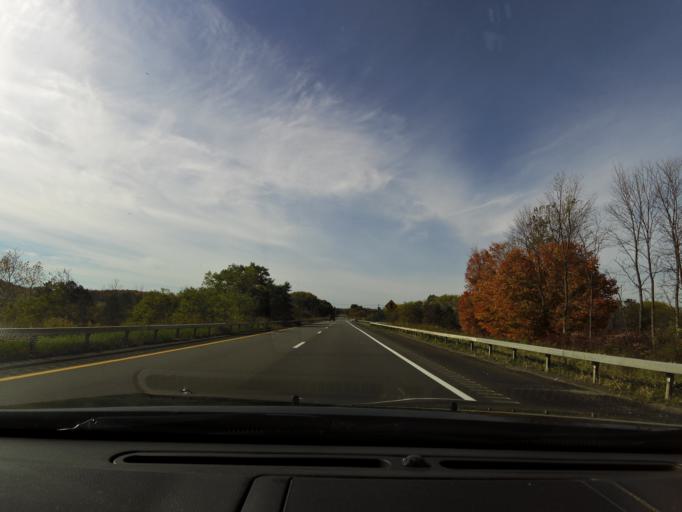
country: US
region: New York
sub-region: Erie County
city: Billington Heights
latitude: 42.7973
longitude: -78.6184
